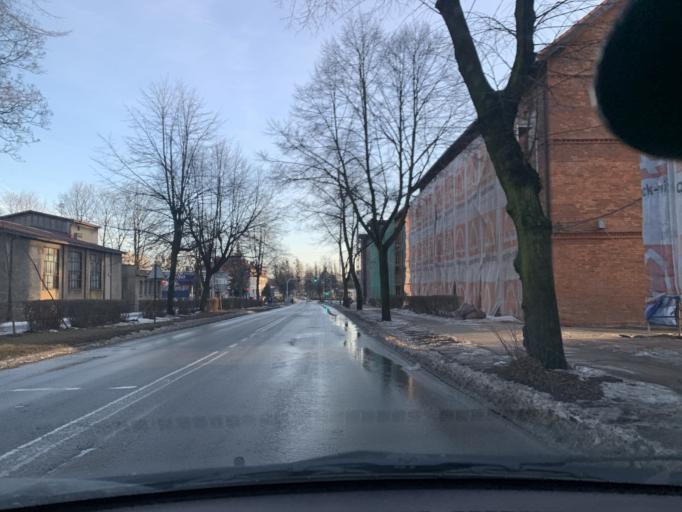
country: PL
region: Silesian Voivodeship
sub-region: Powiat tarnogorski
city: Radzionkow
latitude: 50.3871
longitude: 18.8991
